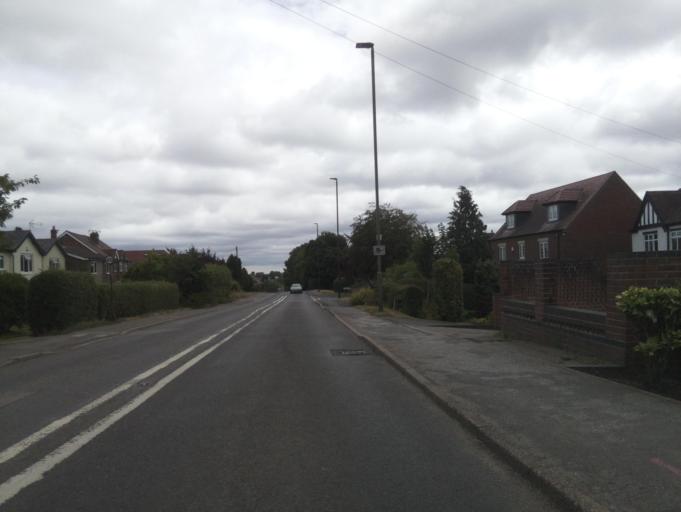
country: GB
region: England
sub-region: Derbyshire
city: Heanor
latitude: 53.0094
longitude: -1.3743
